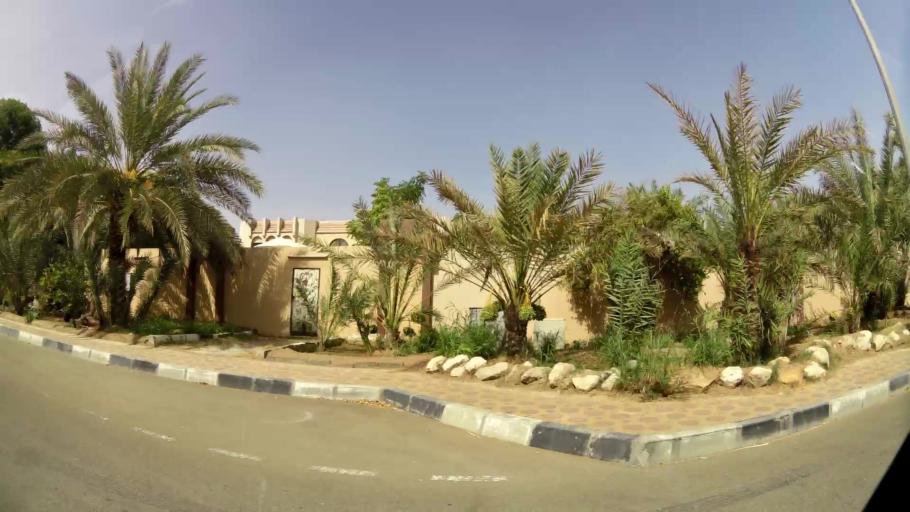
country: AE
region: Abu Dhabi
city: Al Ain
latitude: 24.2333
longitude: 55.6828
